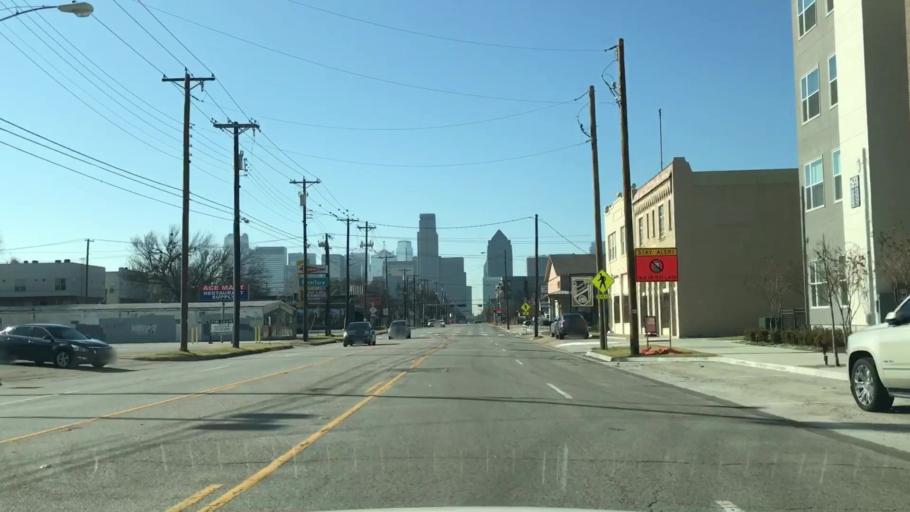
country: US
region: Texas
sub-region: Dallas County
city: Dallas
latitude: 32.7995
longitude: -96.7843
